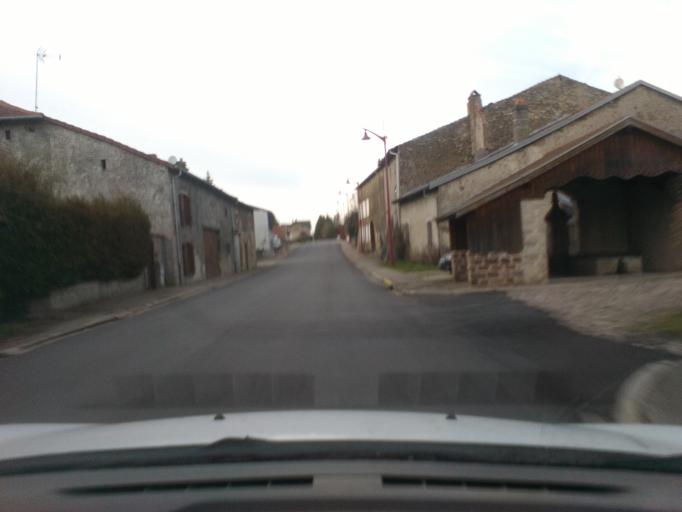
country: FR
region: Lorraine
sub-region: Departement des Vosges
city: Vincey
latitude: 48.3598
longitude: 6.3253
